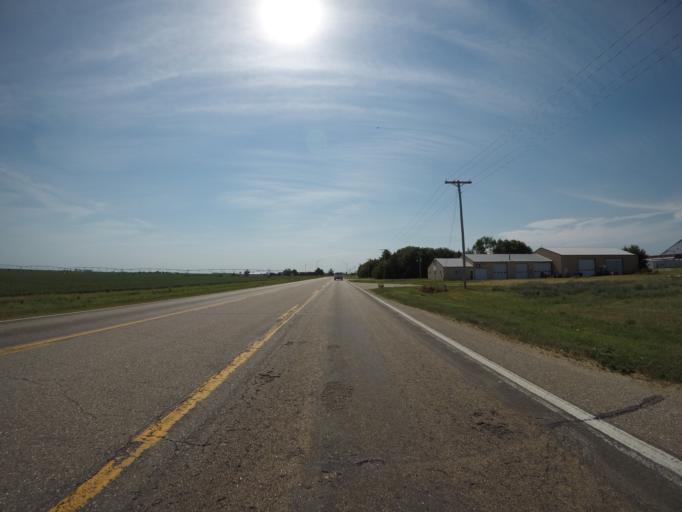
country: US
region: Nebraska
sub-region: Adams County
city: Hastings
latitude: 40.4663
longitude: -98.5564
